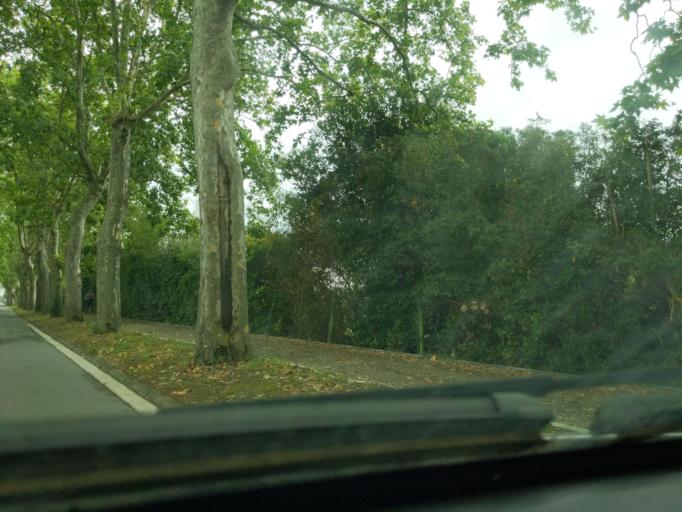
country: FR
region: Midi-Pyrenees
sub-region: Departement de la Haute-Garonne
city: Tournefeuille
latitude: 43.5779
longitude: 1.3609
